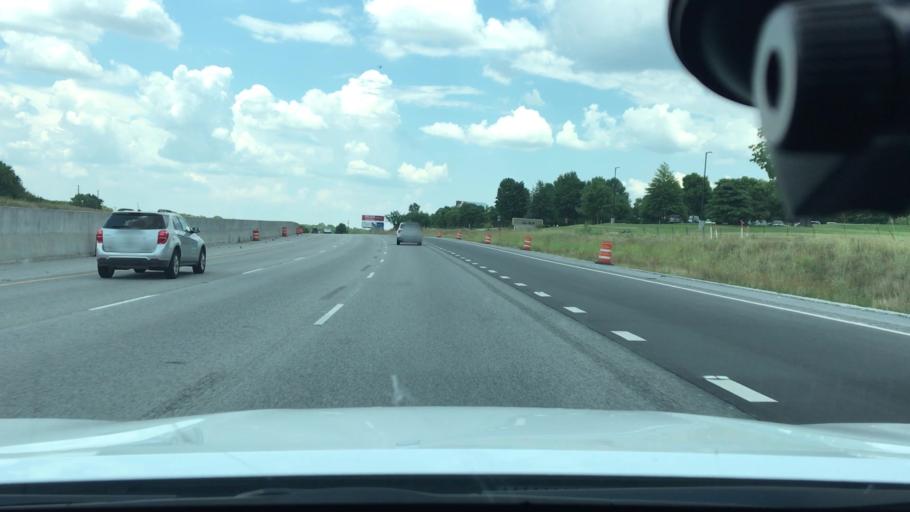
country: US
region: Arkansas
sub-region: Benton County
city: Lowell
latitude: 36.2446
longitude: -94.1515
